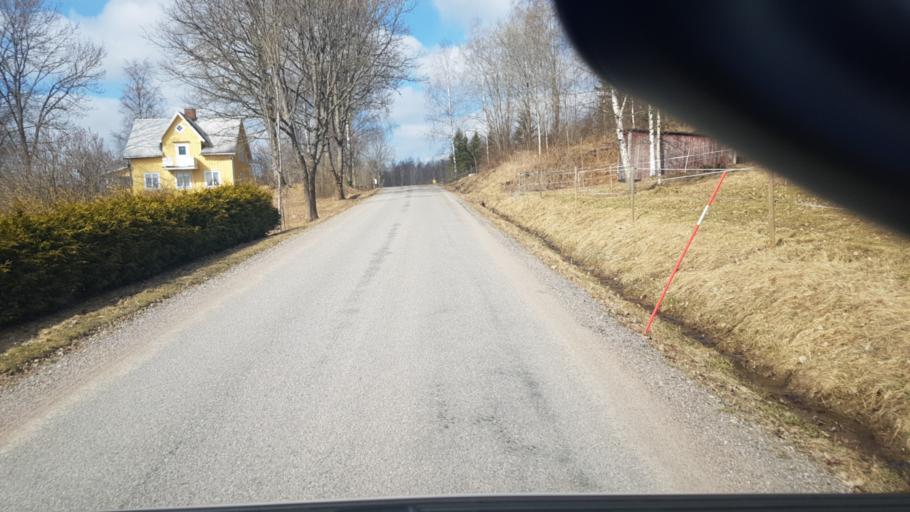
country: SE
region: Vaermland
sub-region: Eda Kommun
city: Amotfors
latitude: 59.7614
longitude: 12.4439
